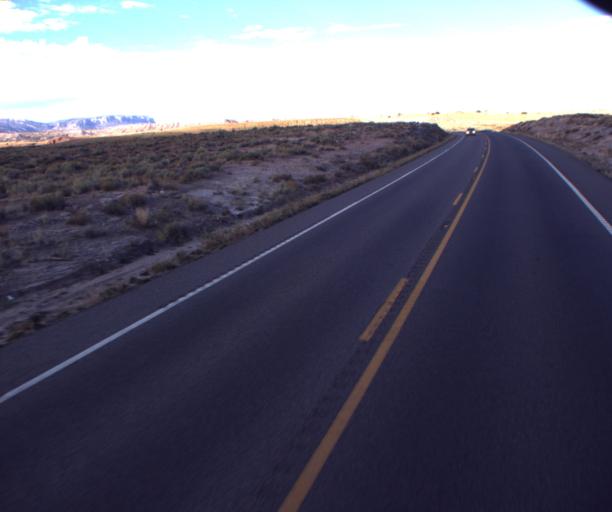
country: US
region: New Mexico
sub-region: San Juan County
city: Shiprock
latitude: 36.9364
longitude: -109.1195
